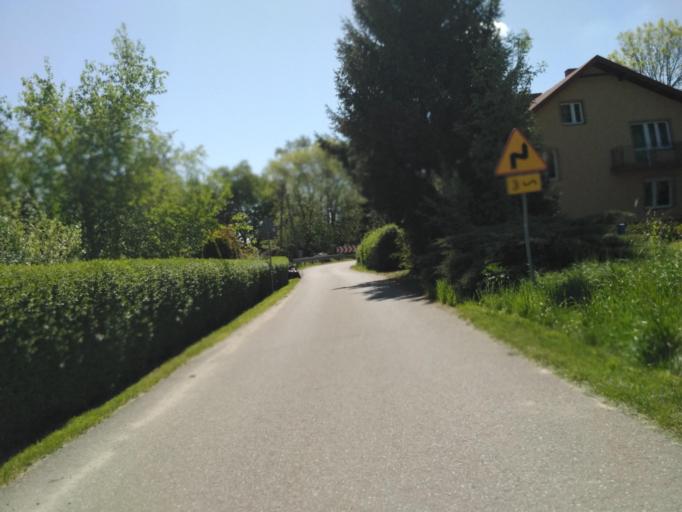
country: PL
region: Subcarpathian Voivodeship
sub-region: Powiat krosnienski
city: Miejsce Piastowe
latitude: 49.6258
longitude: 21.7740
